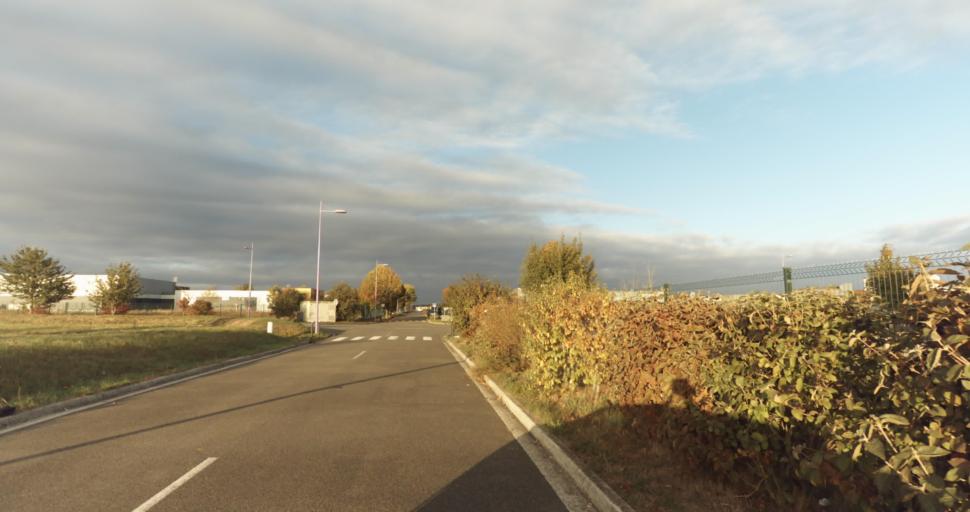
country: FR
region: Centre
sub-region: Departement d'Eure-et-Loir
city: Vernouillet
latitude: 48.7118
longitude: 1.3762
